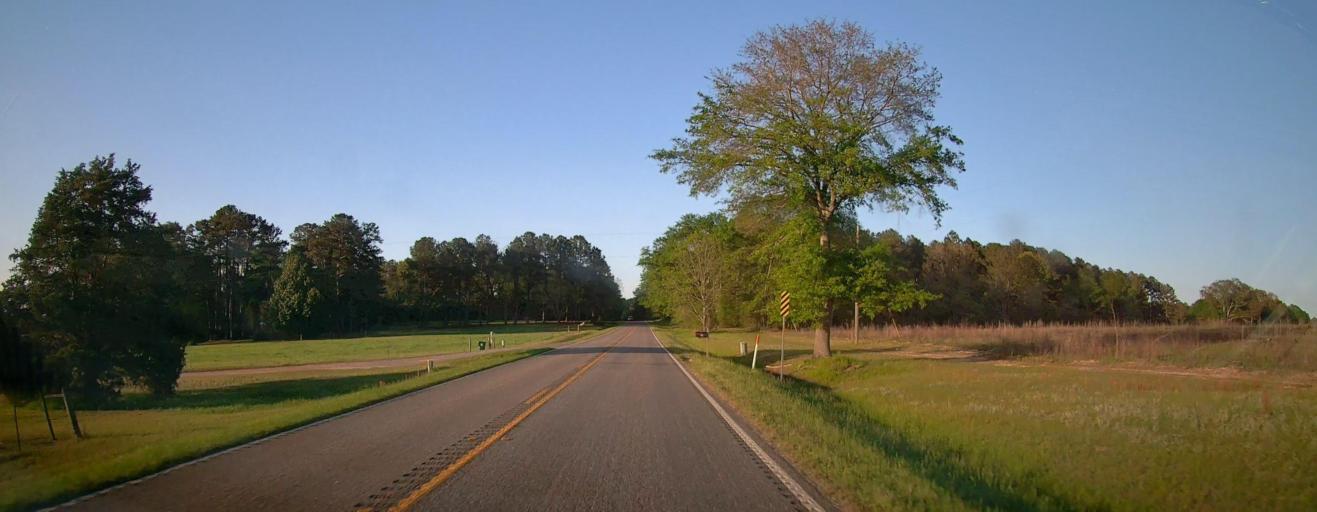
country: US
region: Georgia
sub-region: Marion County
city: Buena Vista
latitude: 32.4021
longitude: -84.4410
